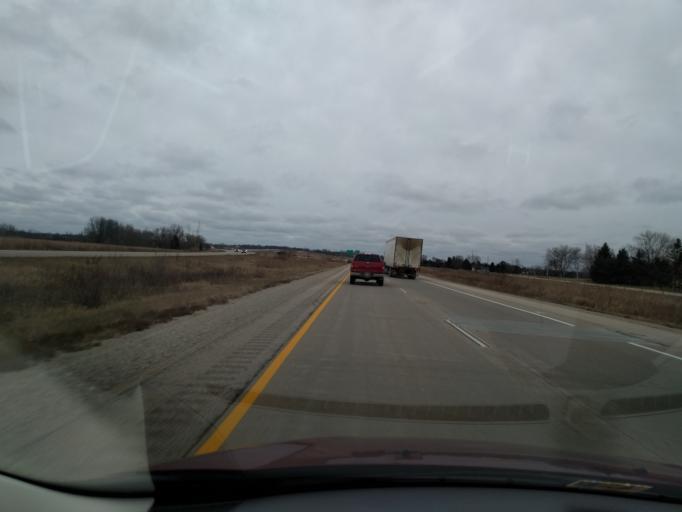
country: US
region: Wisconsin
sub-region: Winnebago County
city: Winneconne
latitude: 44.2127
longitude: -88.6926
